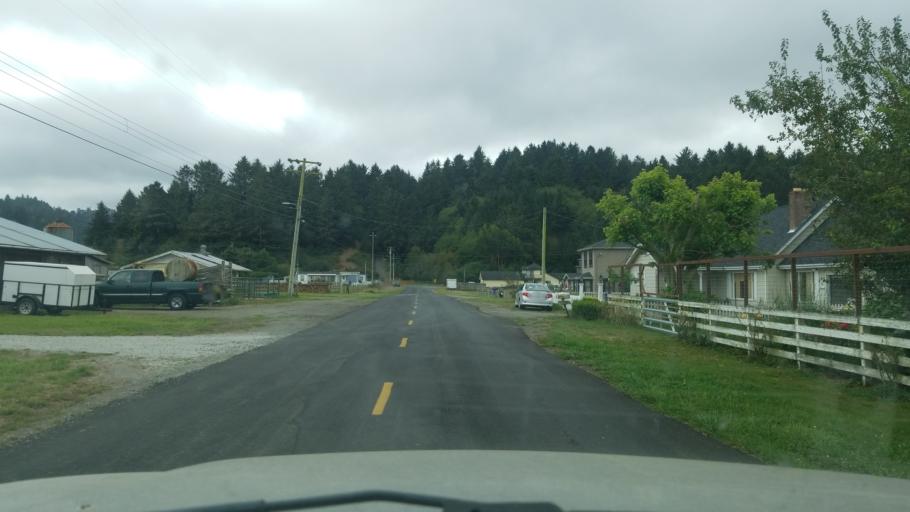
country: US
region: California
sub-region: Humboldt County
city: Ferndale
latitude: 40.5836
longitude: -124.2838
